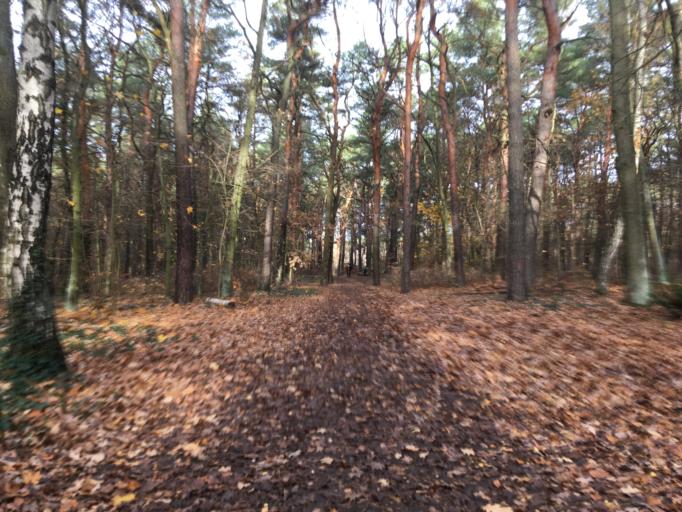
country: DE
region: Berlin
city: Adlershof
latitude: 52.4439
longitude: 13.5416
